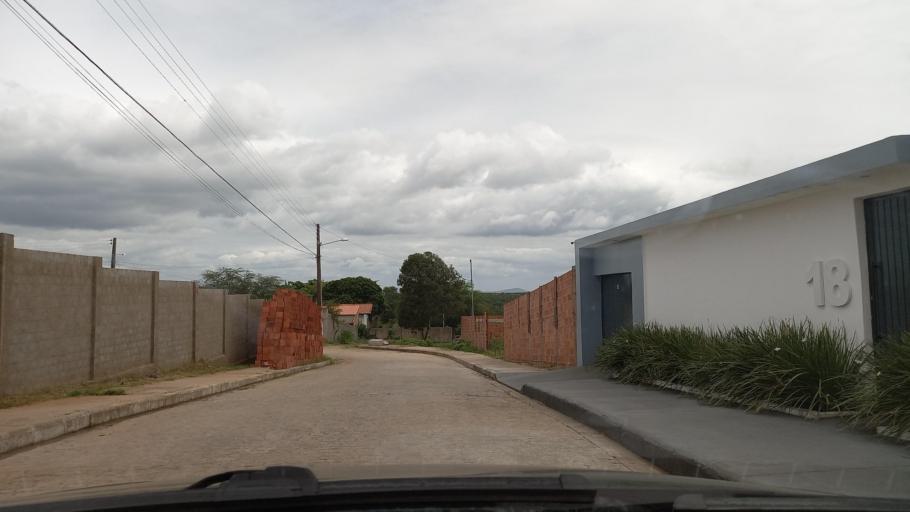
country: BR
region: Sergipe
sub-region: Caninde De Sao Francisco
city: Caninde de Sao Francisco
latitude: -9.6127
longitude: -37.7648
